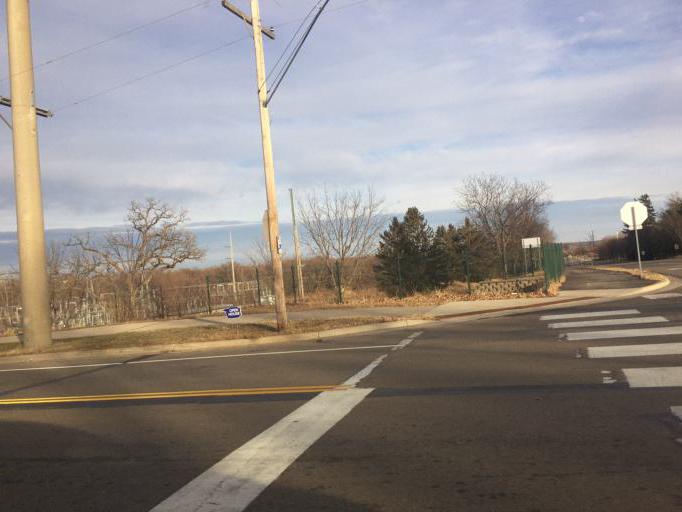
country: US
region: Minnesota
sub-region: Olmsted County
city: Oronoco
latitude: 44.0795
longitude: -92.5388
